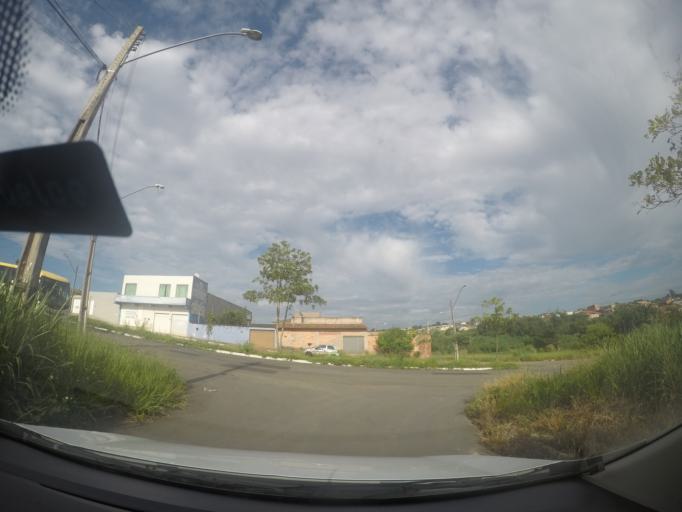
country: BR
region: Goias
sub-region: Goiania
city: Goiania
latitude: -16.6770
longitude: -49.2024
